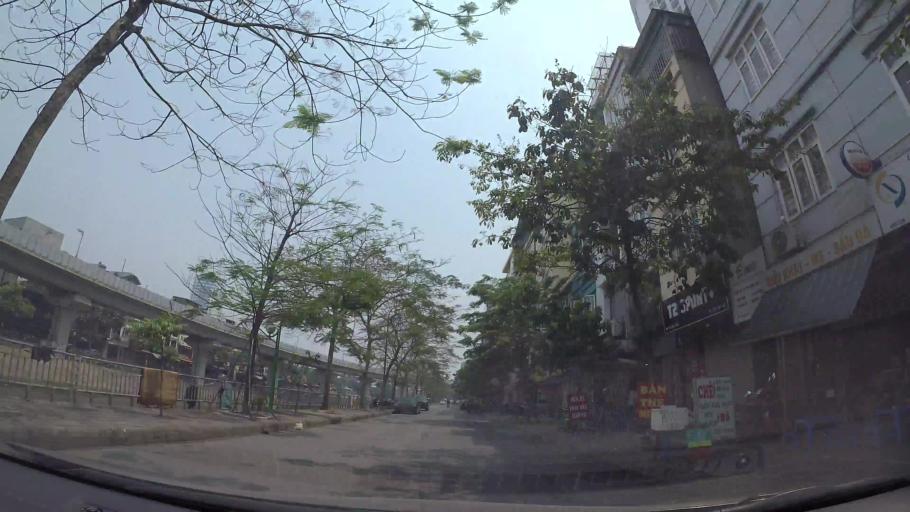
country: VN
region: Ha Noi
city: Thanh Xuan
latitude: 21.0041
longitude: 105.8167
